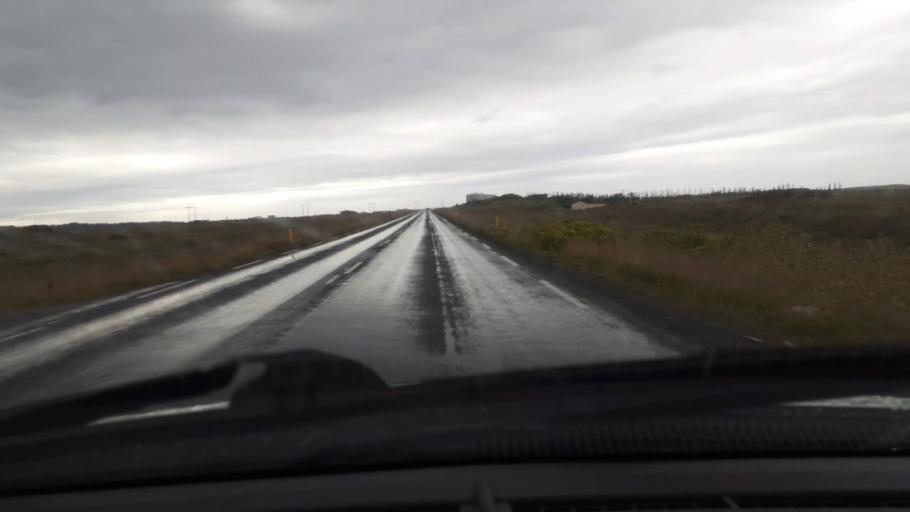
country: IS
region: West
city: Akranes
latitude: 64.3371
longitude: -22.0264
